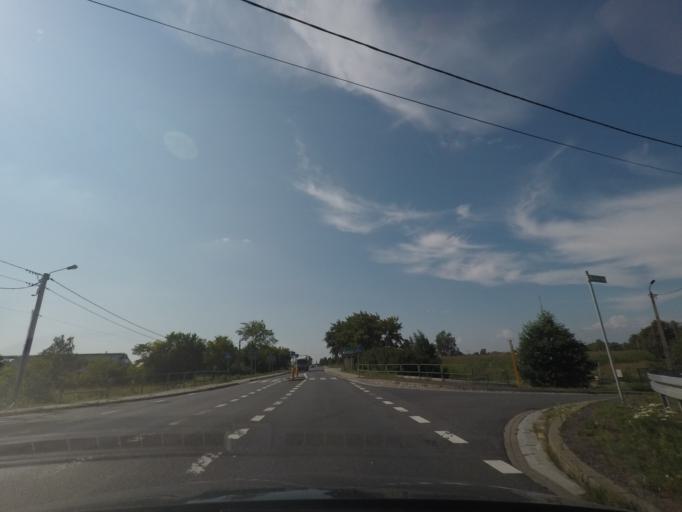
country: PL
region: Silesian Voivodeship
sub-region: Powiat pszczynski
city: Radostowice
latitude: 50.0056
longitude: 18.8715
